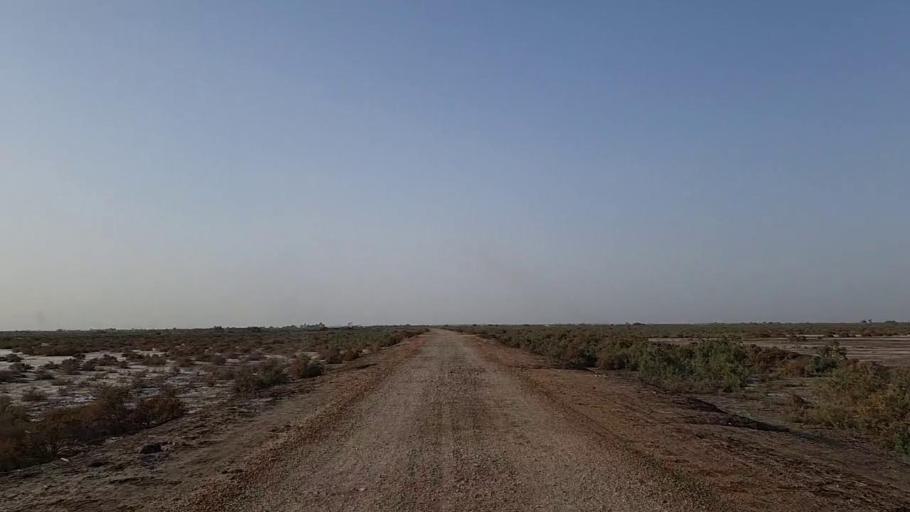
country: PK
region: Sindh
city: Jati
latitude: 24.3579
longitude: 68.1473
